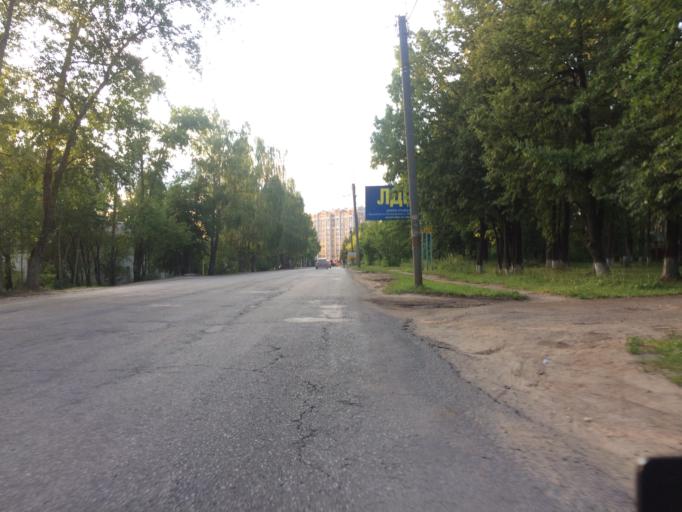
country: RU
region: Mariy-El
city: Yoshkar-Ola
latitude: 56.6290
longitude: 47.9518
